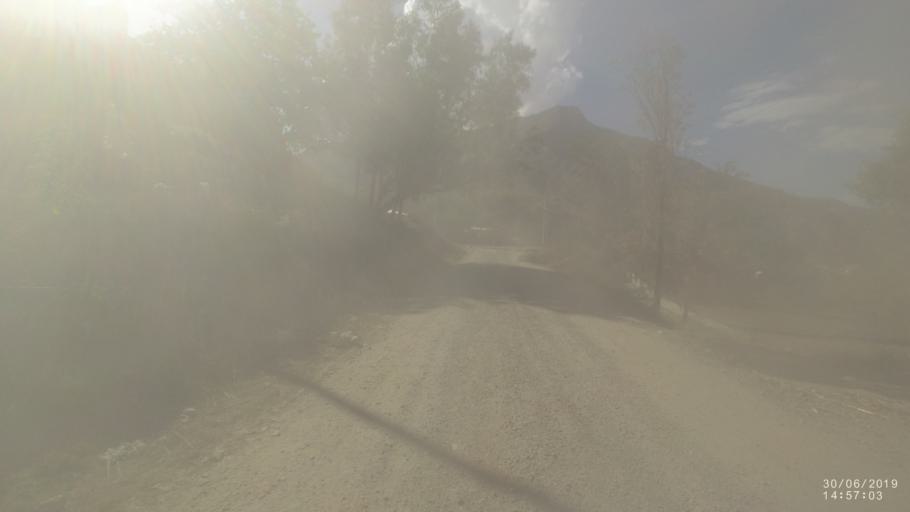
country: BO
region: Cochabamba
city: Irpa Irpa
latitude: -17.7456
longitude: -66.3540
